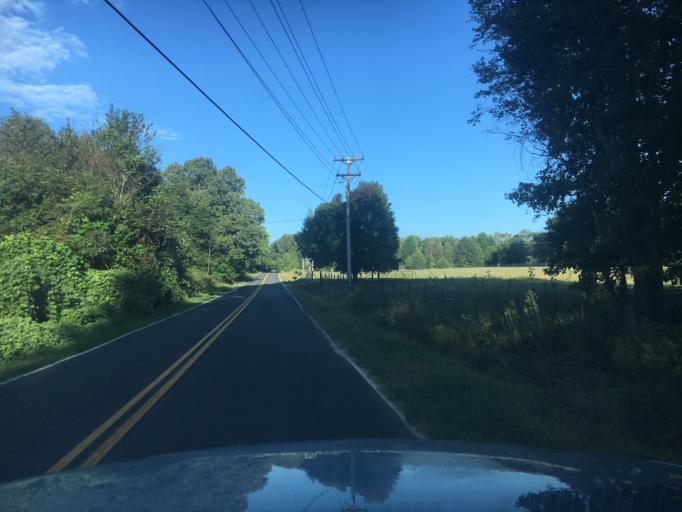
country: US
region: South Carolina
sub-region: Spartanburg County
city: Woodruff
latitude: 34.6304
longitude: -82.0350
